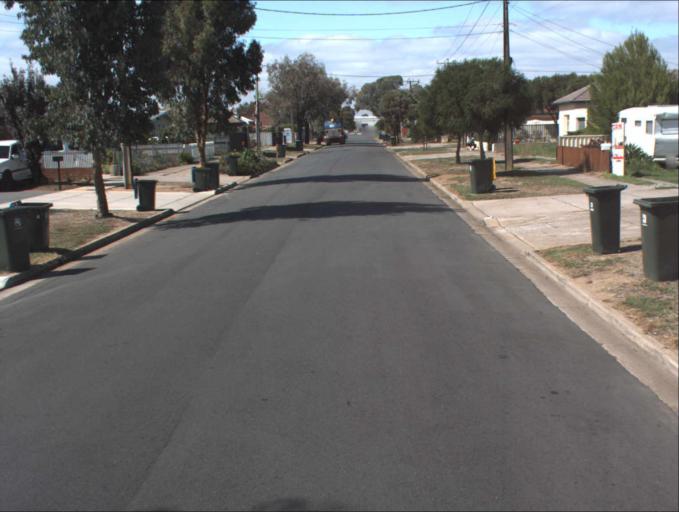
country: AU
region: South Australia
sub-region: Prospect
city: Prospect
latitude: -34.8795
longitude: 138.5770
